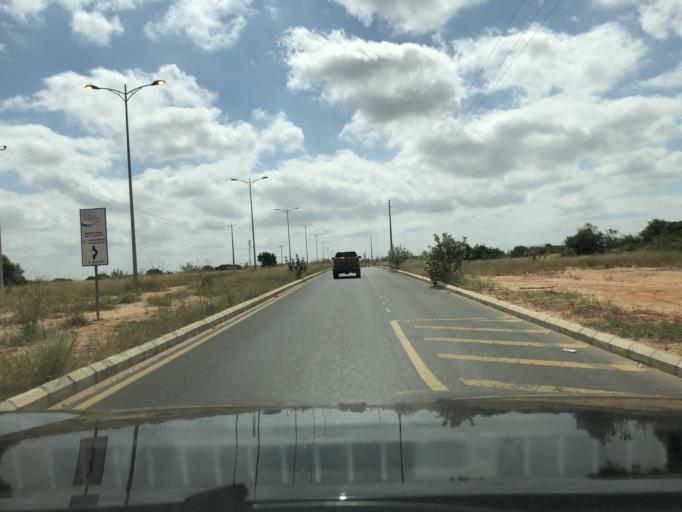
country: AO
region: Luanda
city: Luanda
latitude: -8.9576
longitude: 13.2398
